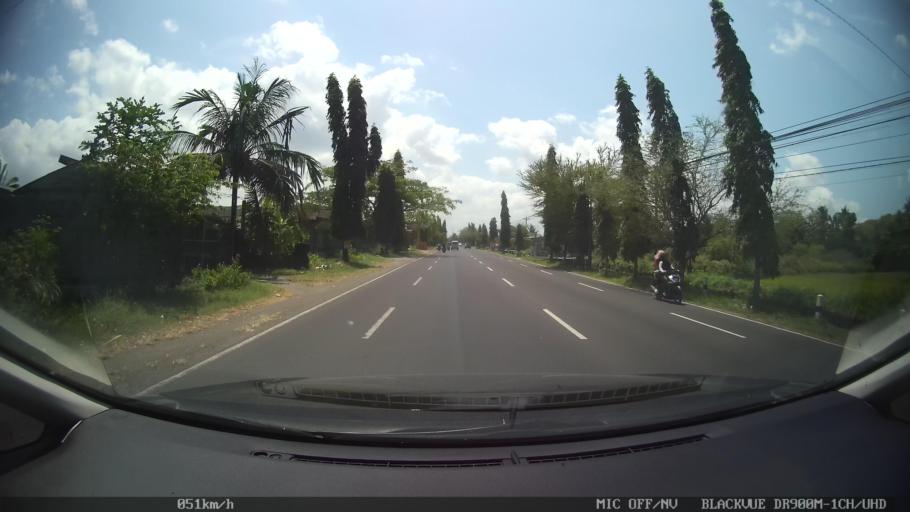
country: ID
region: Daerah Istimewa Yogyakarta
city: Pandak
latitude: -7.9269
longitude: 110.2772
